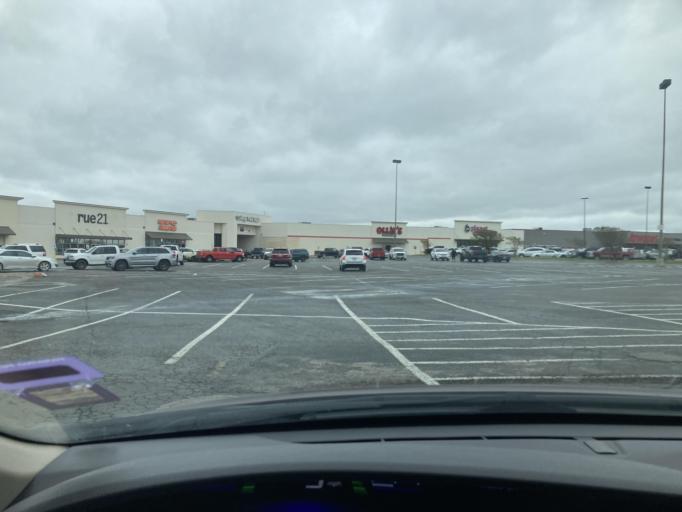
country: US
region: Texas
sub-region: Navarro County
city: Corsicana
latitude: 32.0776
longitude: -96.5078
